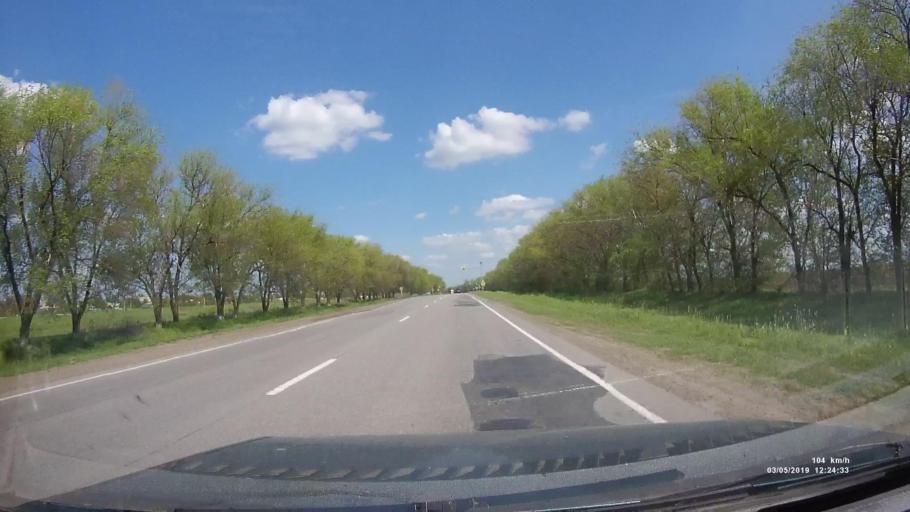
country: RU
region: Rostov
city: Semikarakorsk
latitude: 47.4214
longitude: 40.7009
